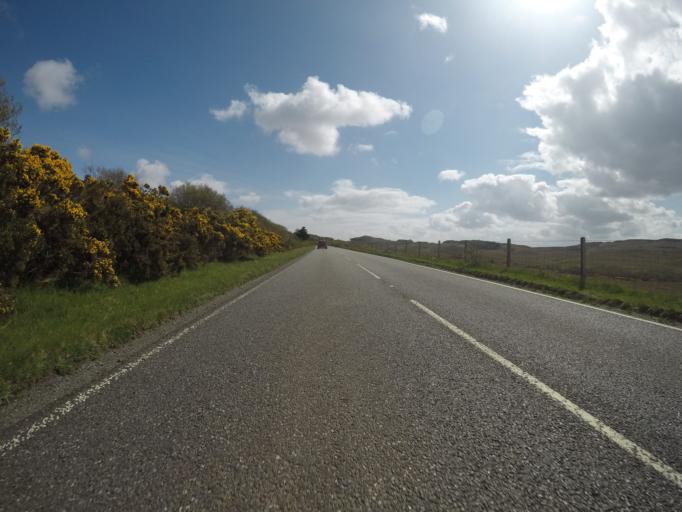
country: GB
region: Scotland
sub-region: Highland
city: Portree
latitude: 57.5245
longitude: -6.3443
